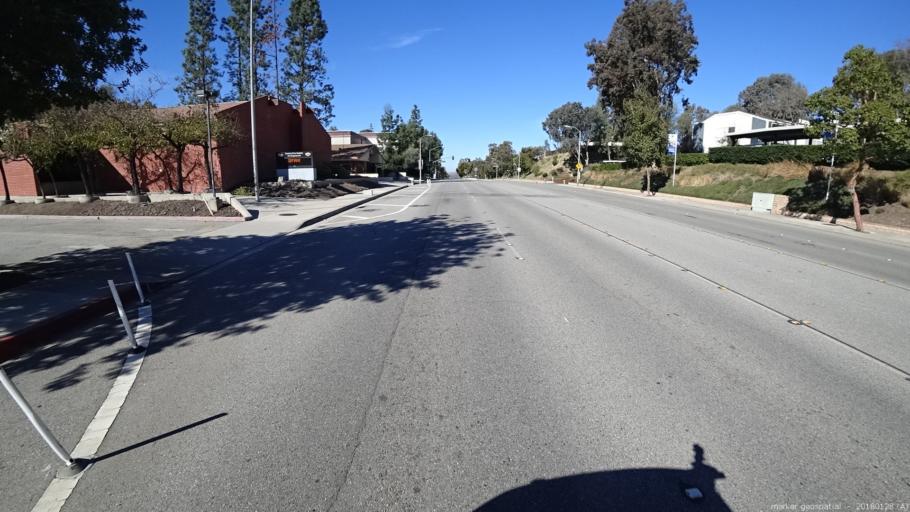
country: US
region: California
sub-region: Los Angeles County
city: Diamond Bar
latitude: 34.0019
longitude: -117.8135
